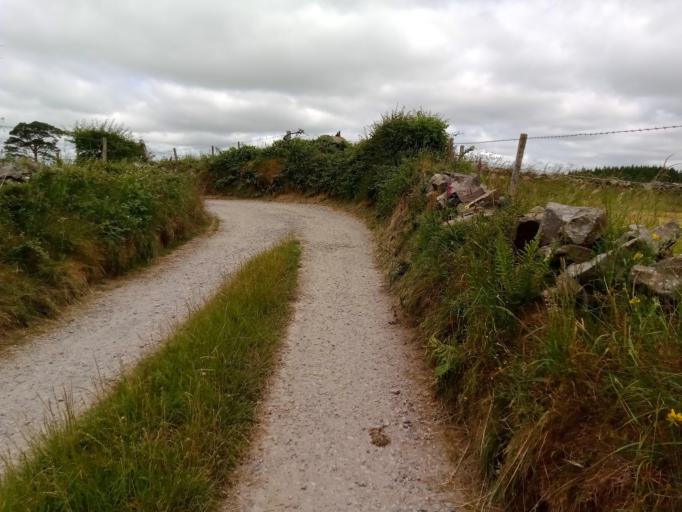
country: IE
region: Leinster
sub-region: Laois
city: Rathdowney
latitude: 52.7963
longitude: -7.4643
